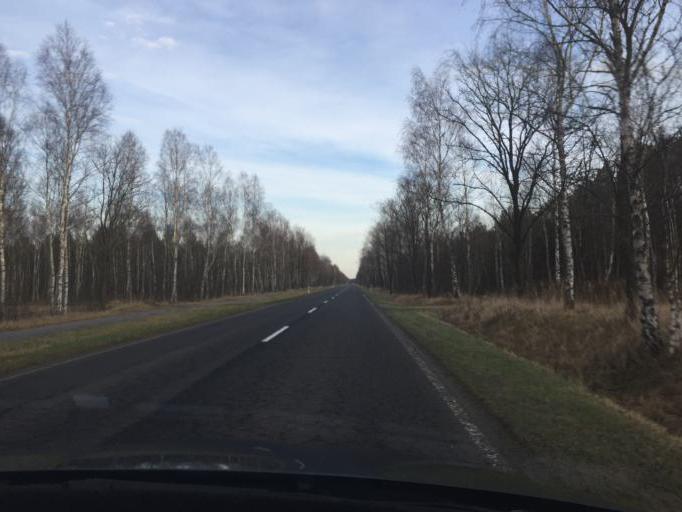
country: DE
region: Brandenburg
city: Forst
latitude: 51.7485
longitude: 14.6898
